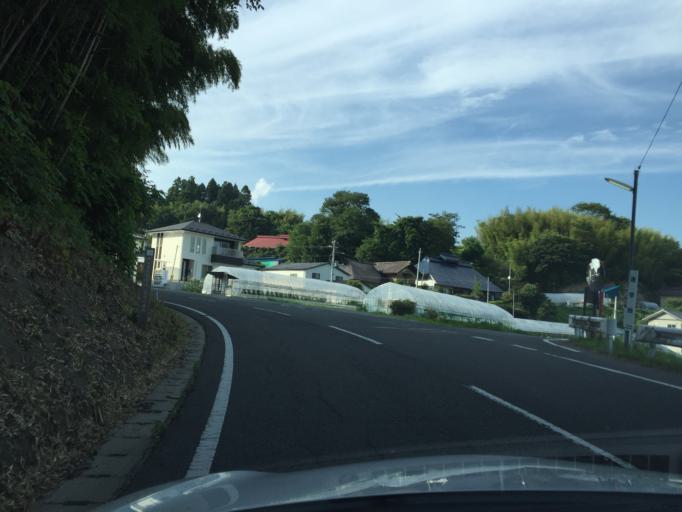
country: JP
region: Fukushima
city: Miharu
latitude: 37.4265
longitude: 140.5006
